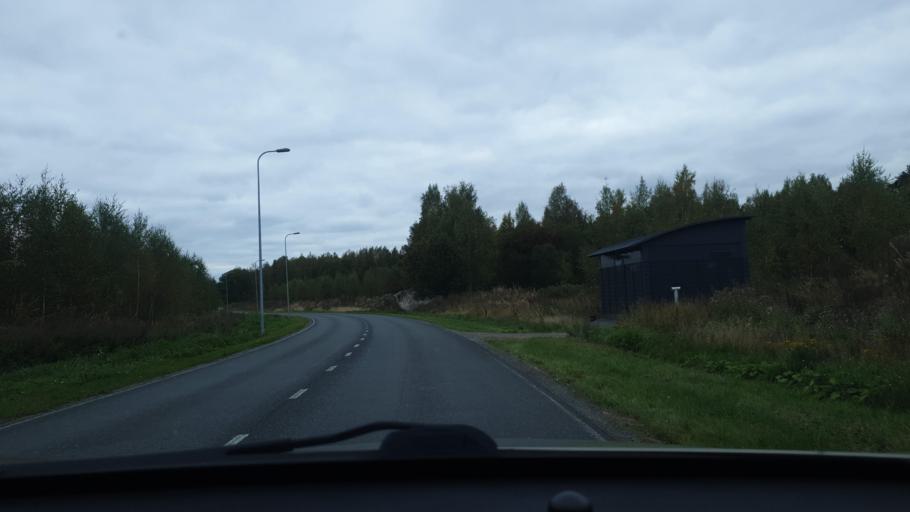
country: FI
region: Ostrobothnia
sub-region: Vaasa
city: Teeriniemi
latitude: 63.1011
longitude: 21.6940
